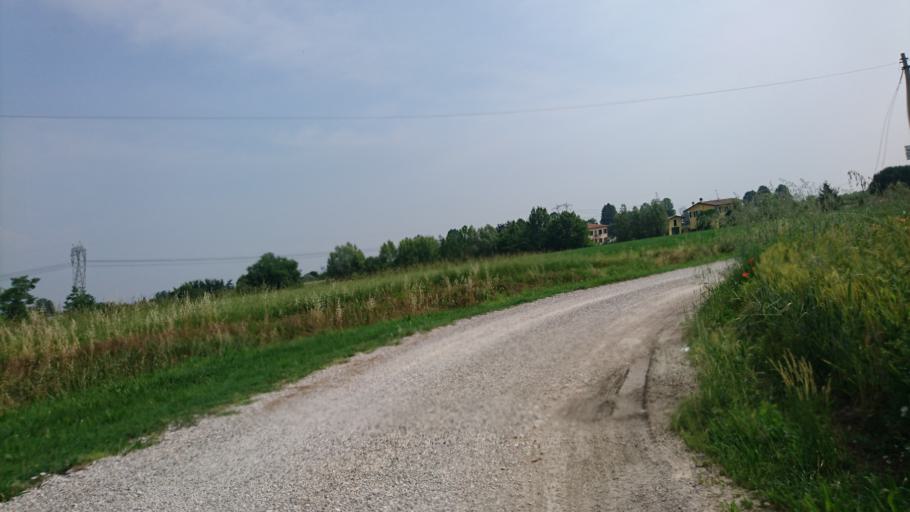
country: IT
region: Veneto
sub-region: Provincia di Padova
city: Ponte San Nicolo
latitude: 45.3557
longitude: 11.9410
